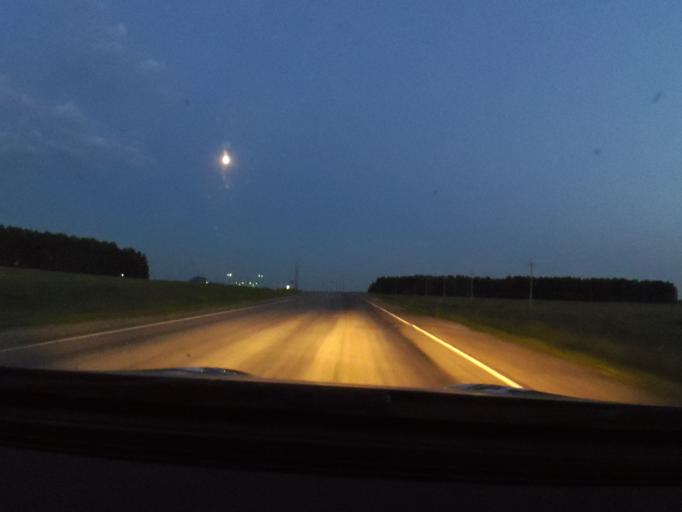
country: RU
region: Bashkortostan
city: Duvan
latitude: 55.9527
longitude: 58.1975
